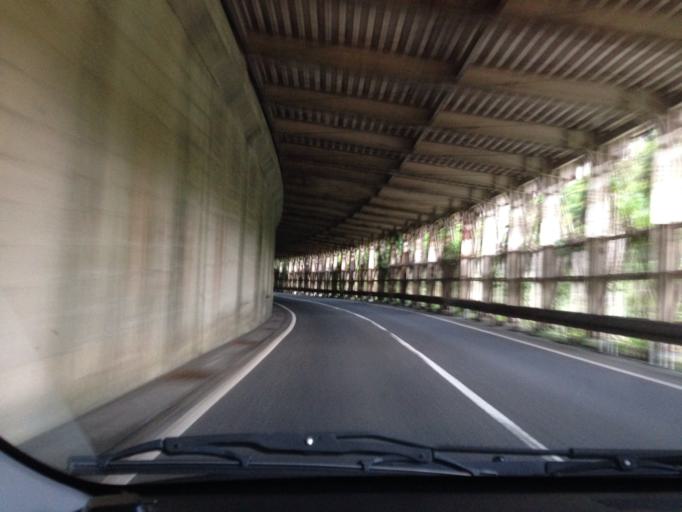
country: JP
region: Fukushima
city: Kitakata
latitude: 37.4806
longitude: 139.6899
